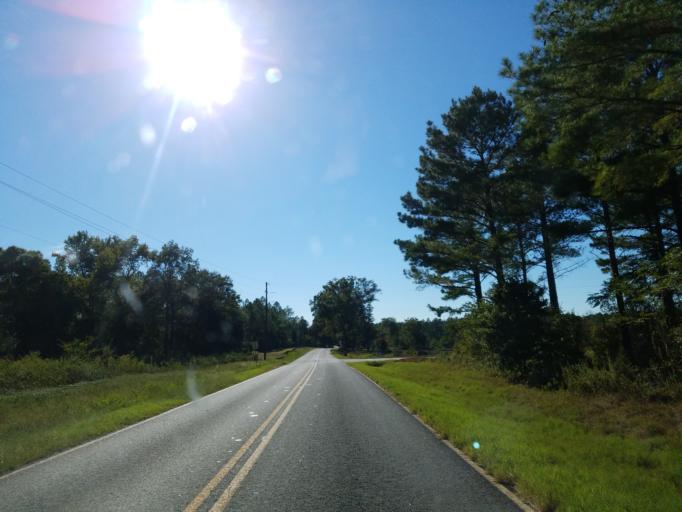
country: US
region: Georgia
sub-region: Dooly County
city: Unadilla
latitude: 32.2416
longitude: -83.8549
